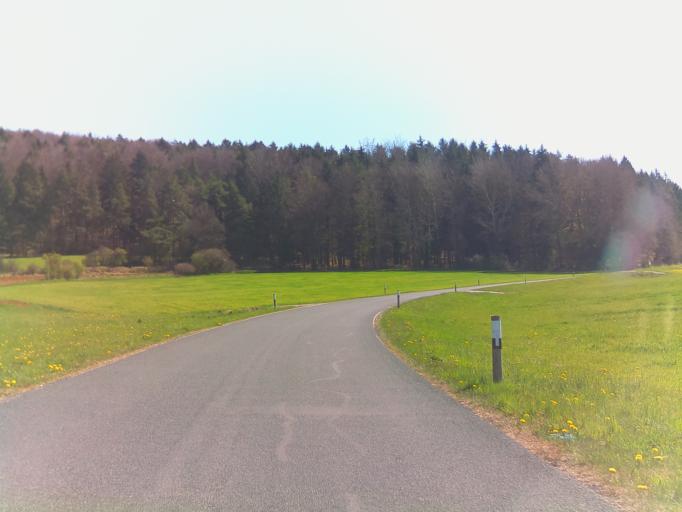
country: DE
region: Bavaria
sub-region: Regierungsbezirk Mittelfranken
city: Alfeld
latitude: 49.4121
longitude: 11.5751
